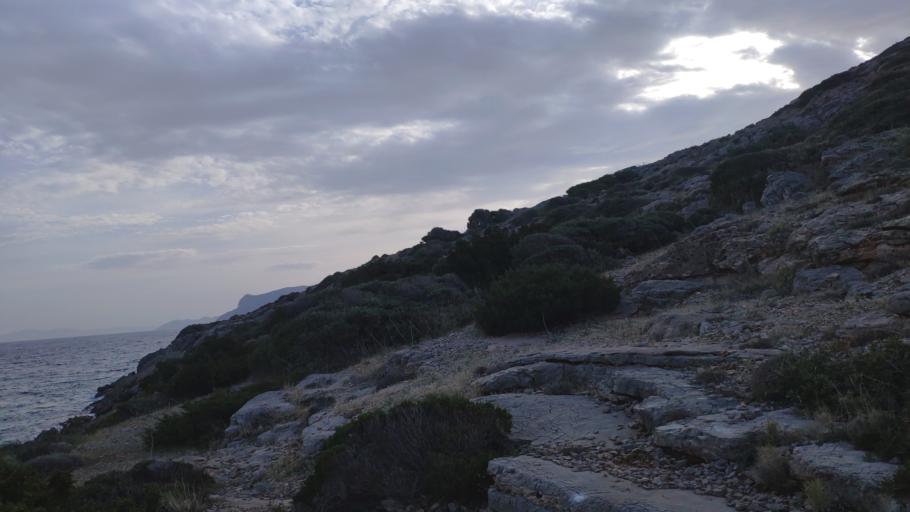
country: GR
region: Attica
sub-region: Nomarchia Anatolikis Attikis
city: Limin Mesoyaias
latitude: 37.9025
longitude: 24.0449
